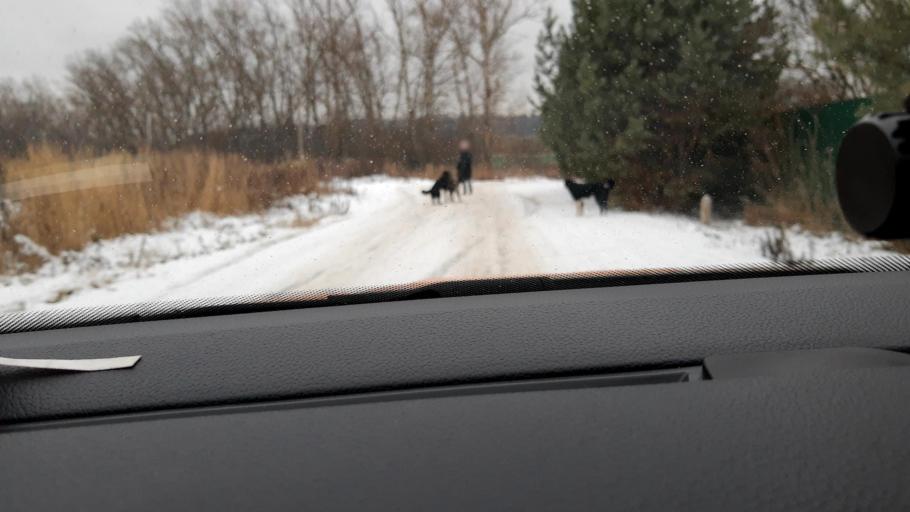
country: RU
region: Moskovskaya
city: Pirogovskiy
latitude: 55.9614
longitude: 37.7212
